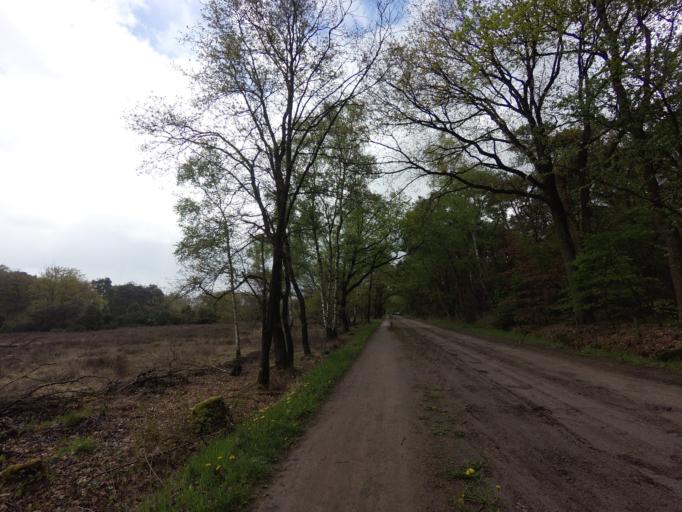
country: NL
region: Overijssel
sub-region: Gemeente Haaksbergen
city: Haaksbergen
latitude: 52.1522
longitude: 6.8055
